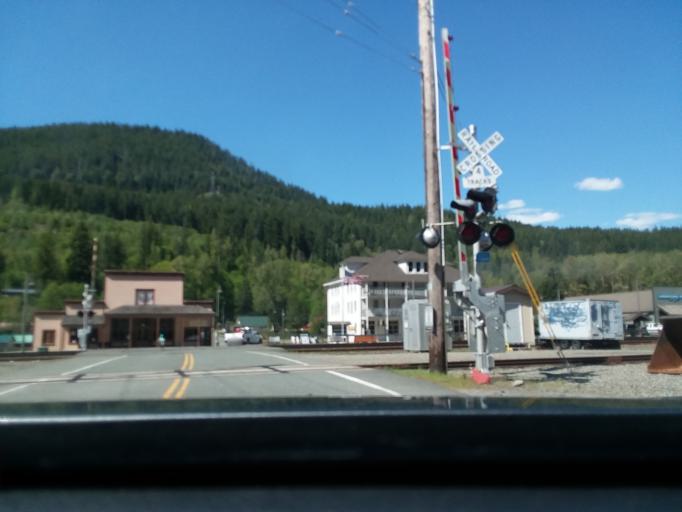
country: US
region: Washington
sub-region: Snohomish County
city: Gold Bar
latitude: 47.7087
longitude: -121.3608
